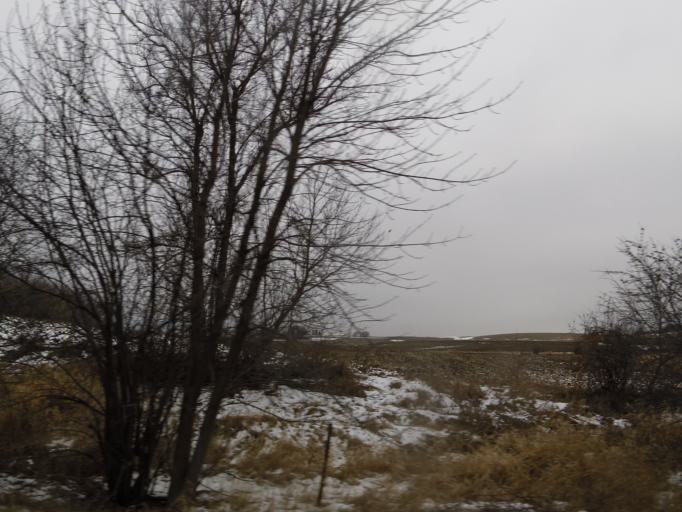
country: US
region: Minnesota
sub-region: Carver County
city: Cologne
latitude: 44.7912
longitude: -93.7881
